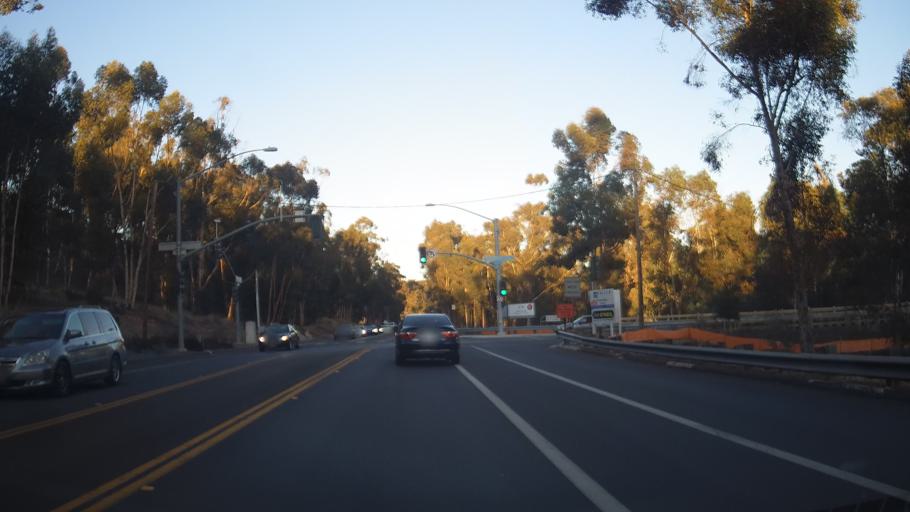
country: US
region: California
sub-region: San Diego County
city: Poway
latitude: 32.9034
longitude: -117.0894
